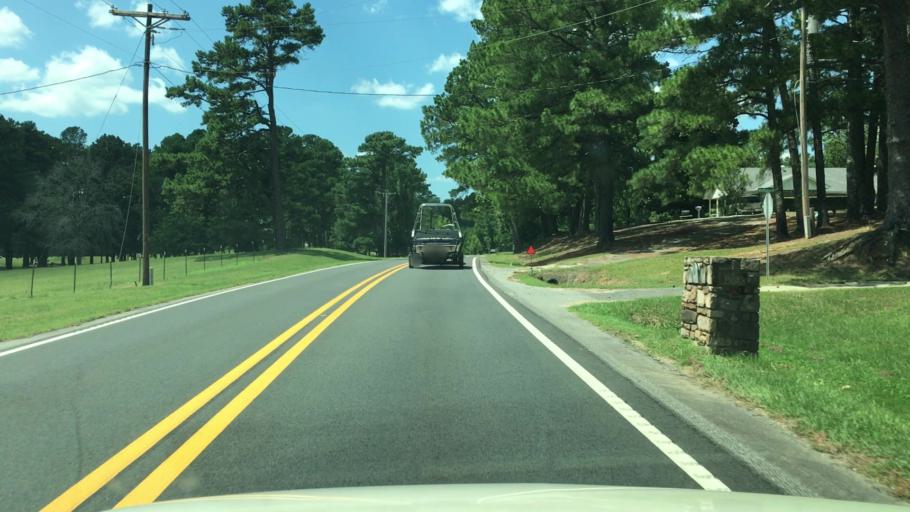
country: US
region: Arkansas
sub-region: Clark County
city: Arkadelphia
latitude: 34.2524
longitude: -93.1225
